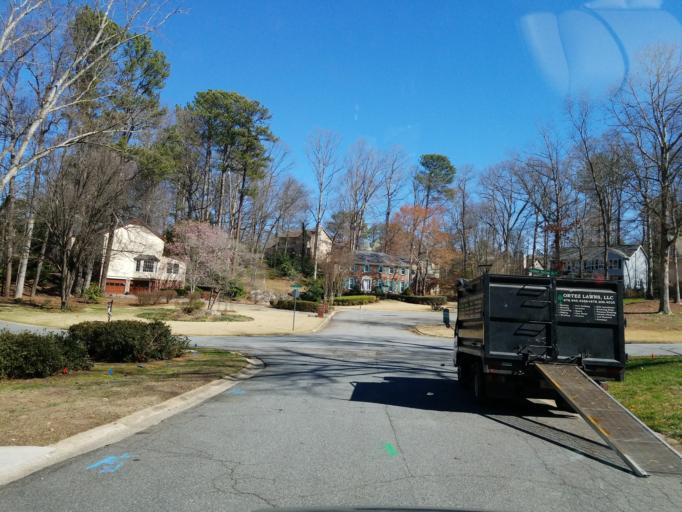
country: US
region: Georgia
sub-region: Fulton County
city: Sandy Springs
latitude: 33.9728
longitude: -84.4484
